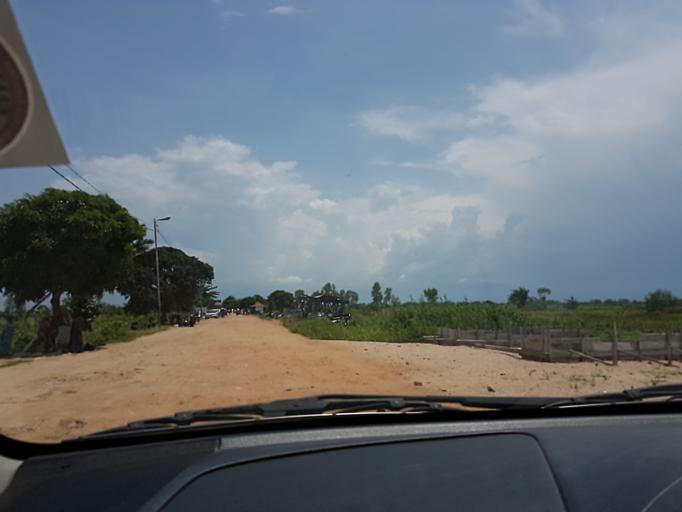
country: CD
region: South Kivu
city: Uvira
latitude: -3.3395
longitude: 29.2095
